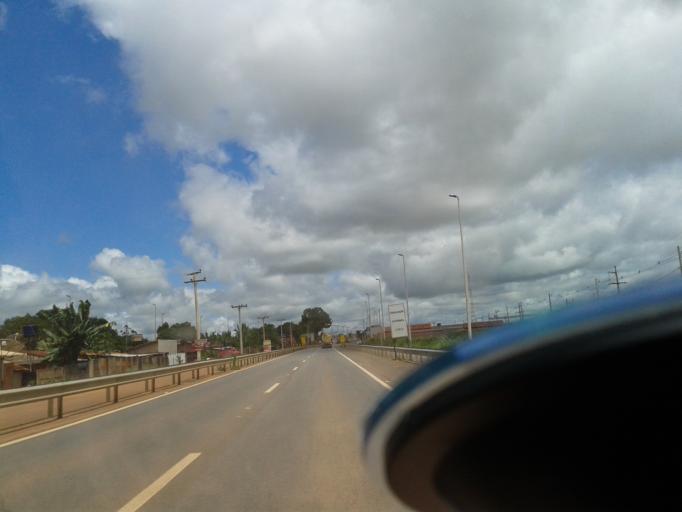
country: BR
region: Goias
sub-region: Itaberai
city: Itaberai
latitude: -16.0507
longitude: -49.7867
